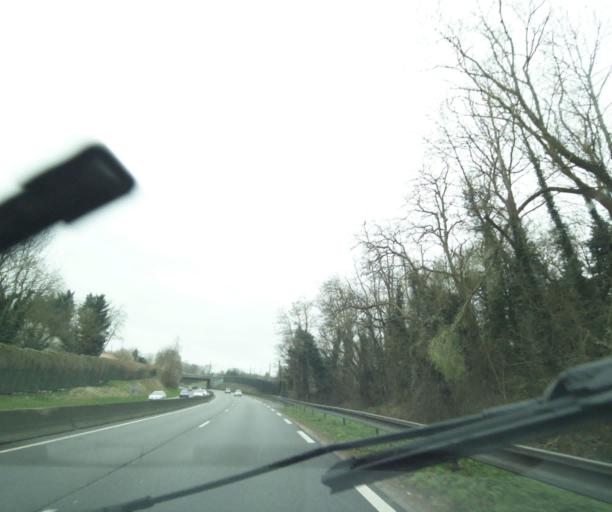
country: FR
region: Ile-de-France
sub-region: Departement de l'Essonne
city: Arpajon
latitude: 48.5883
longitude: 2.2352
